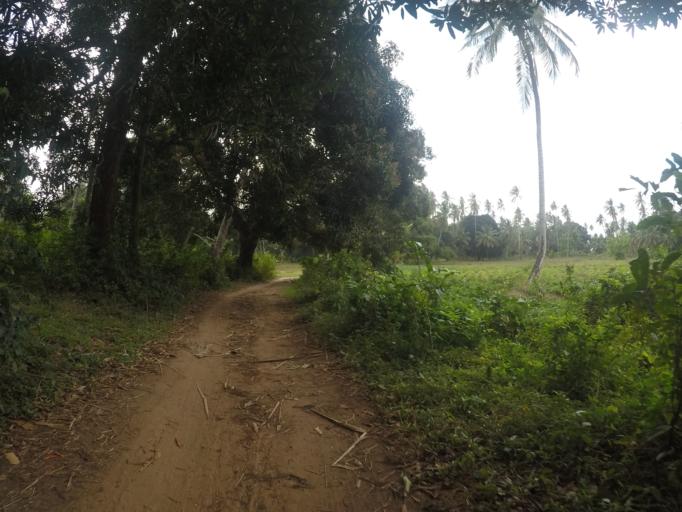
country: TZ
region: Zanzibar Urban/West
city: Zanzibar
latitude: -6.2060
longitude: 39.2350
